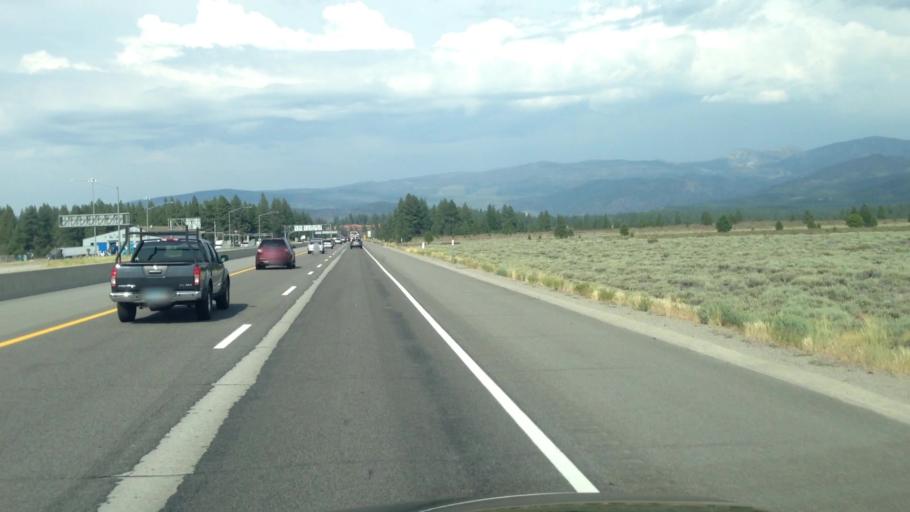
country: US
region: California
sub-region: Nevada County
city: Truckee
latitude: 39.3603
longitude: -120.1353
